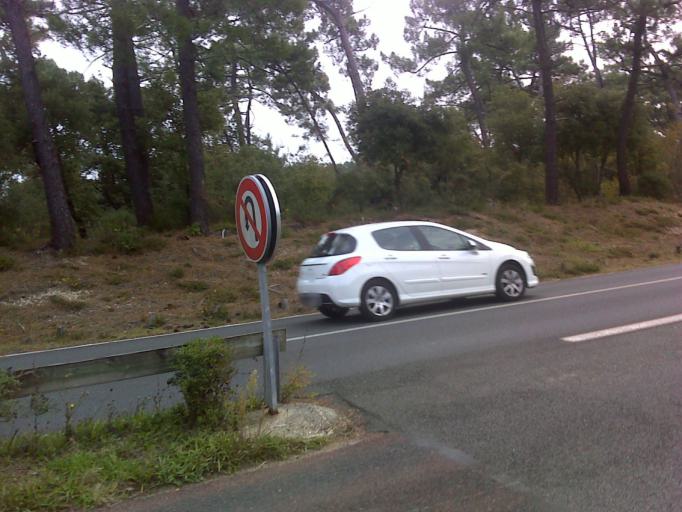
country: FR
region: Poitou-Charentes
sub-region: Departement de la Charente-Maritime
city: Saint-Palais-sur-Mer
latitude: 45.6576
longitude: -1.1256
